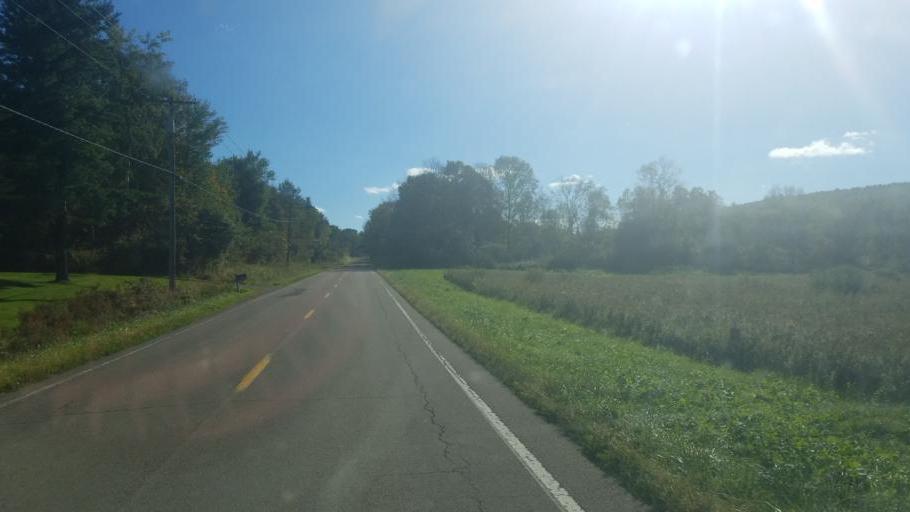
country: US
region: New York
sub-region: Allegany County
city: Friendship
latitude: 42.3035
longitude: -78.1111
